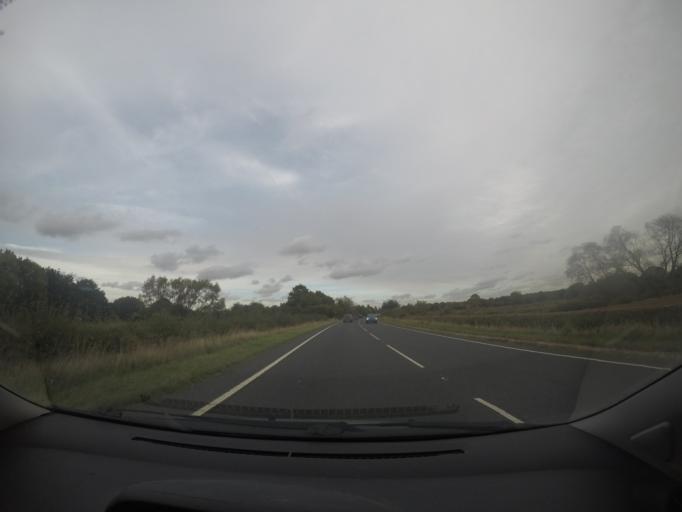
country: GB
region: England
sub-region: North Yorkshire
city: Riccall
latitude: 53.8423
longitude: -1.0559
